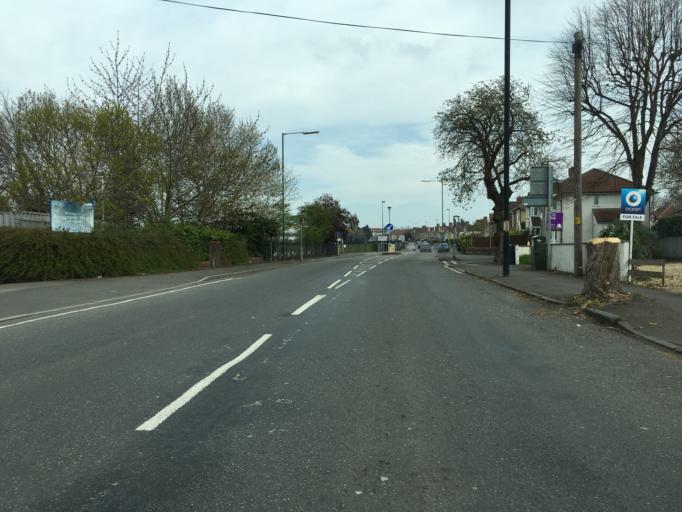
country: GB
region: England
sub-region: Bristol
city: Bristol
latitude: 51.5033
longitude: -2.5881
